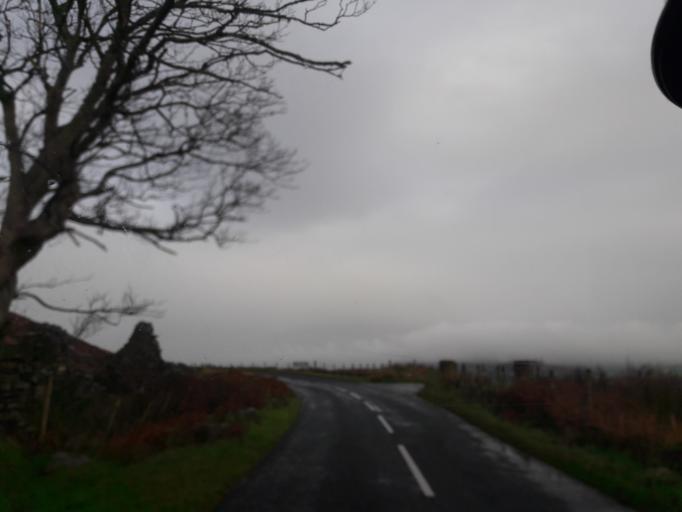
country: IE
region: Ulster
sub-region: County Donegal
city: Buncrana
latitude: 55.1772
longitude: -7.5781
